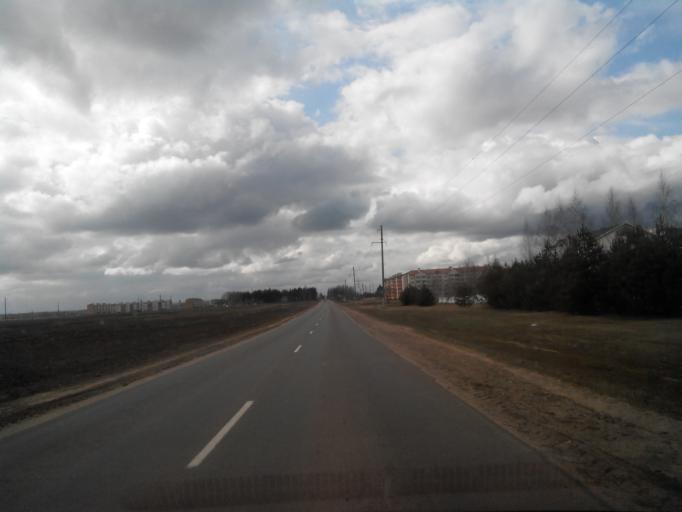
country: BY
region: Vitebsk
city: Pastavy
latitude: 55.1122
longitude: 26.8872
